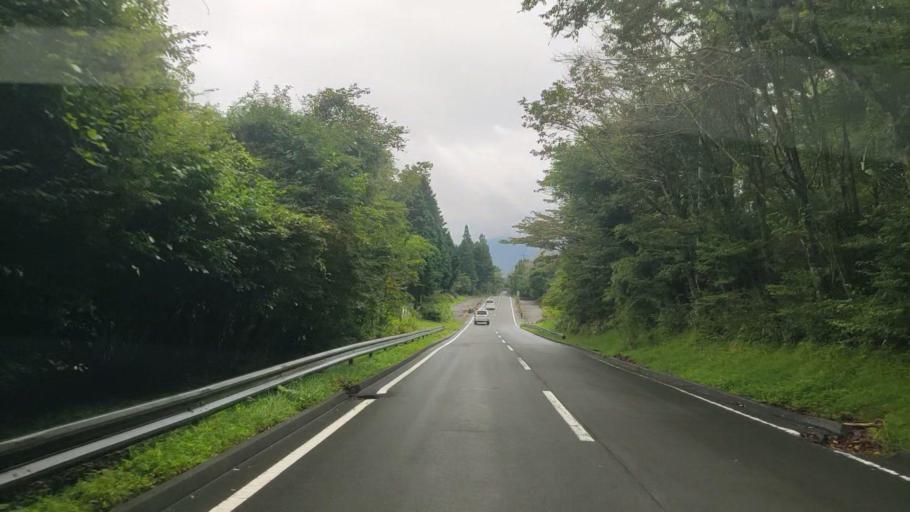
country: JP
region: Shizuoka
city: Gotemba
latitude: 35.2802
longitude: 138.7941
